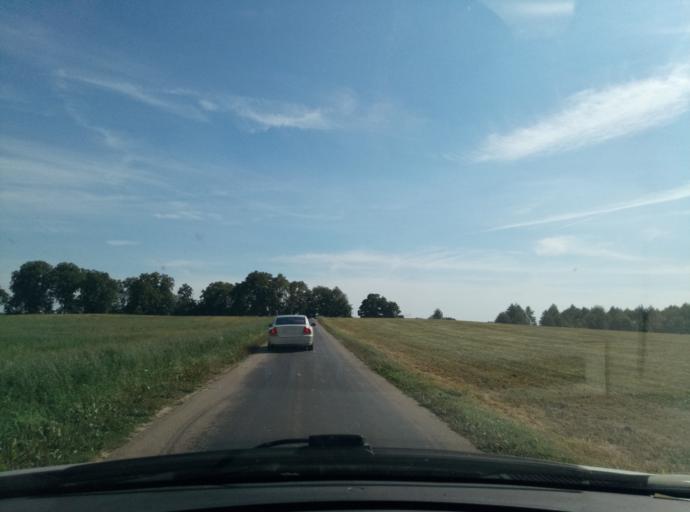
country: PL
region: Kujawsko-Pomorskie
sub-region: Powiat brodnicki
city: Jablonowo Pomorskie
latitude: 53.4111
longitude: 19.2370
